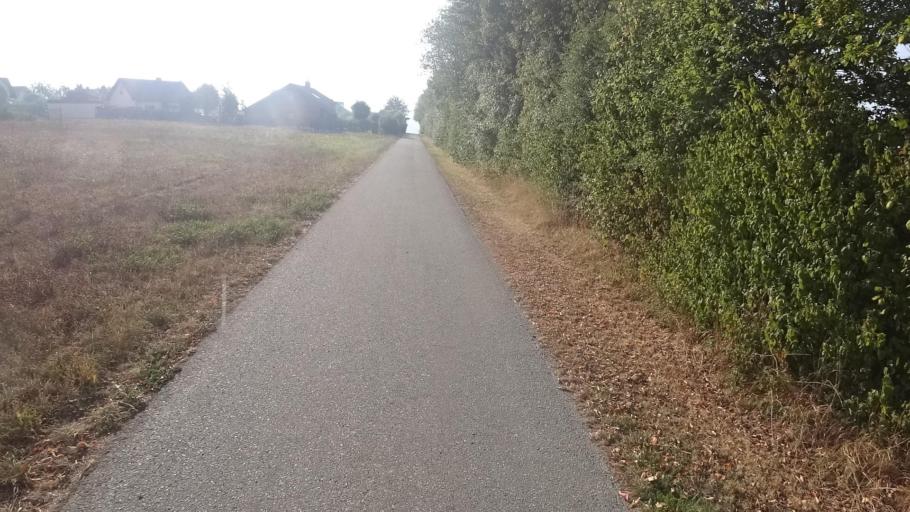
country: DE
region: Rheinland-Pfalz
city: Tiefenbach
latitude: 49.9571
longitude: 7.5519
